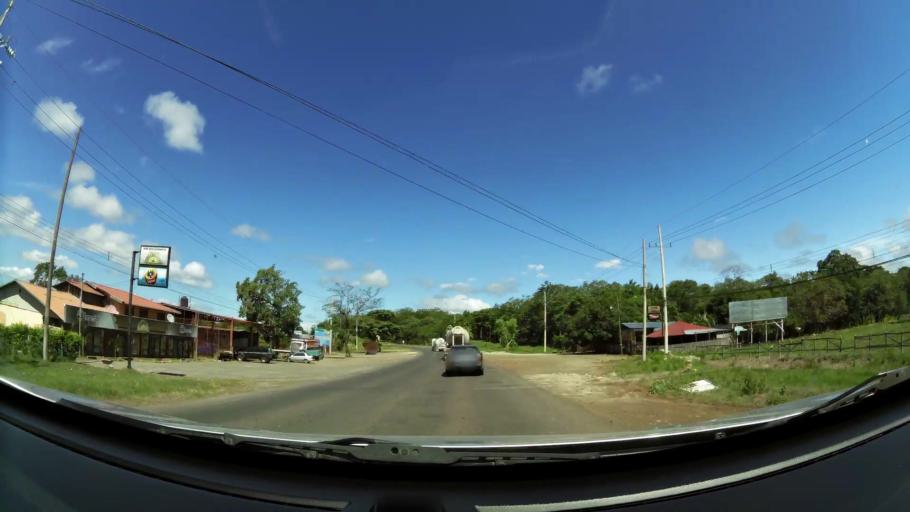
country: CR
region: Guanacaste
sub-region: Canton de Canas
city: Canas
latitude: 10.4110
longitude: -85.0851
